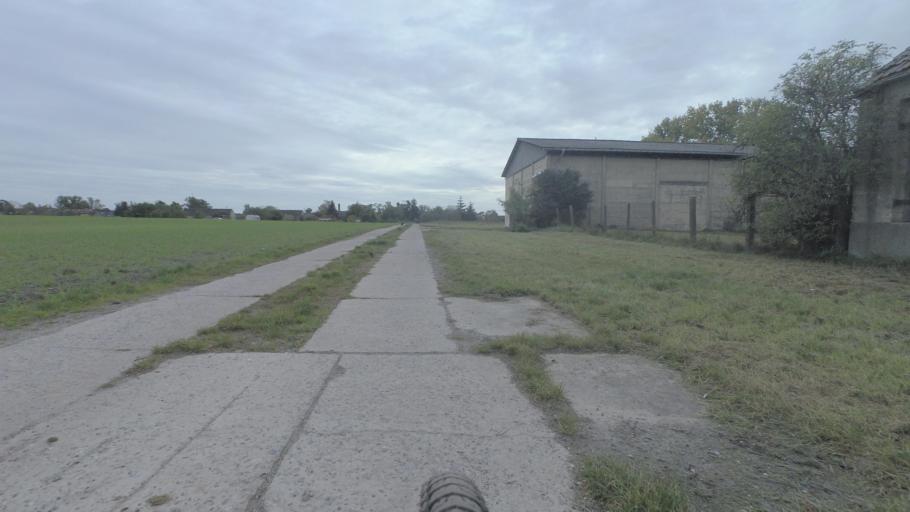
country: DE
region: Brandenburg
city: Rangsdorf
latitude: 52.2762
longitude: 13.3501
